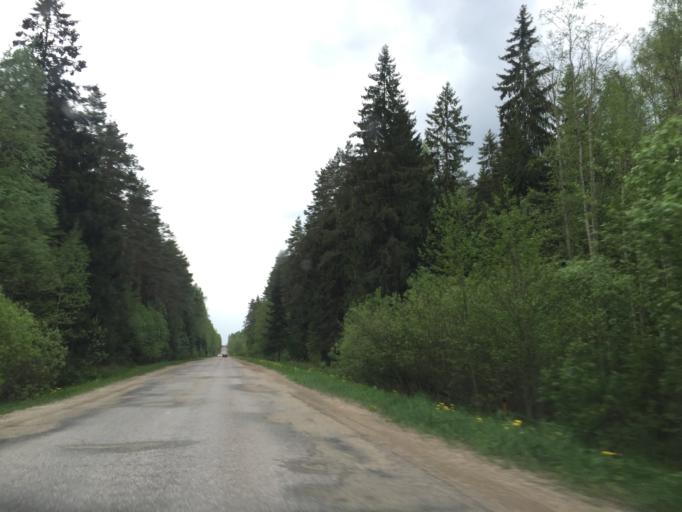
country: LV
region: Ogre
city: Ogre
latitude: 56.8530
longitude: 24.5681
